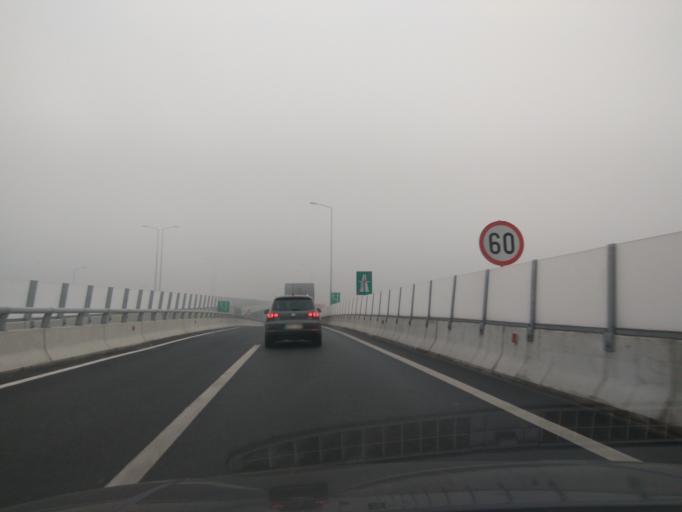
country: BA
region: Federation of Bosnia and Herzegovina
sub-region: Kanton Sarajevo
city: Sarajevo
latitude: 43.8513
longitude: 18.3233
